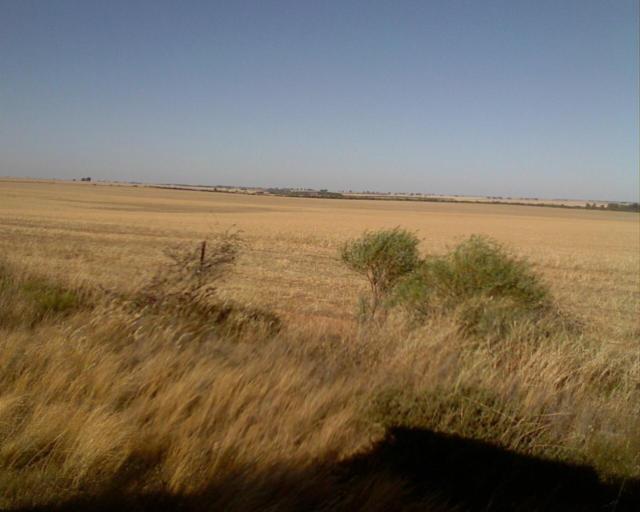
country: AU
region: Western Australia
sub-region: Moora
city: Moora
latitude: -30.2498
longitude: 116.3835
